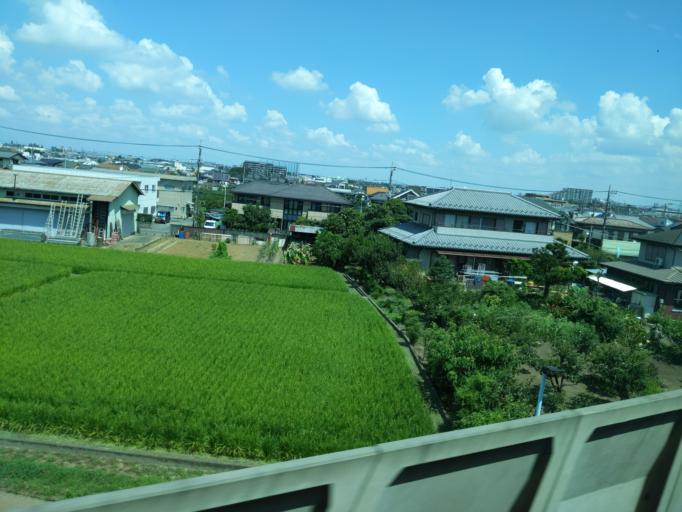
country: JP
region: Tokyo
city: Chofugaoka
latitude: 35.6429
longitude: 139.5104
